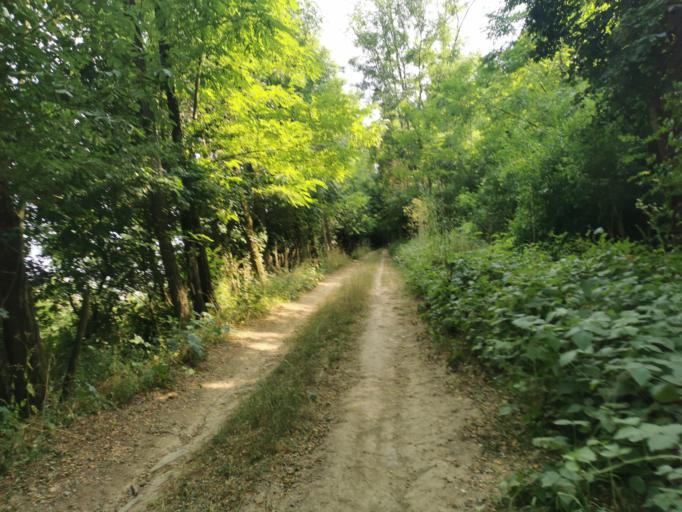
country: SK
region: Trnavsky
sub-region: Okres Senica
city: Senica
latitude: 48.7022
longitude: 17.4280
